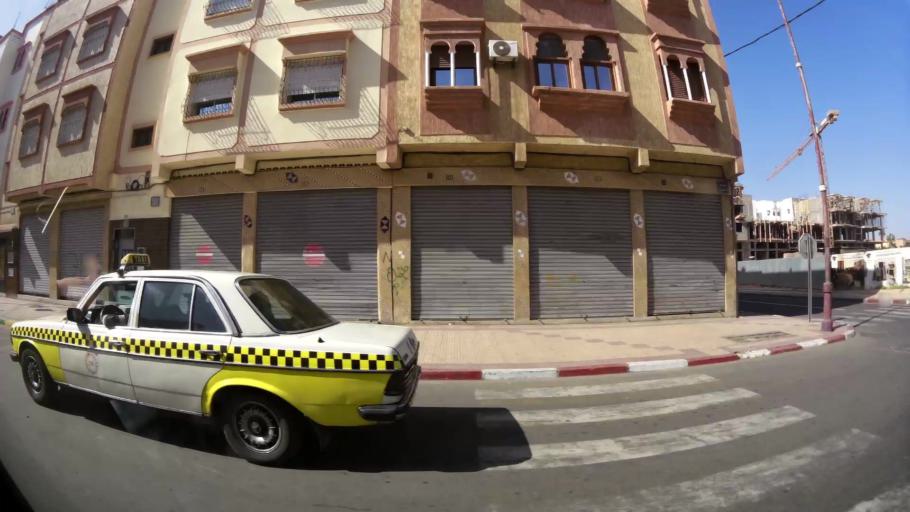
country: MA
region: Souss-Massa-Draa
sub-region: Inezgane-Ait Mellou
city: Inezgane
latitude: 30.3718
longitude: -9.5478
